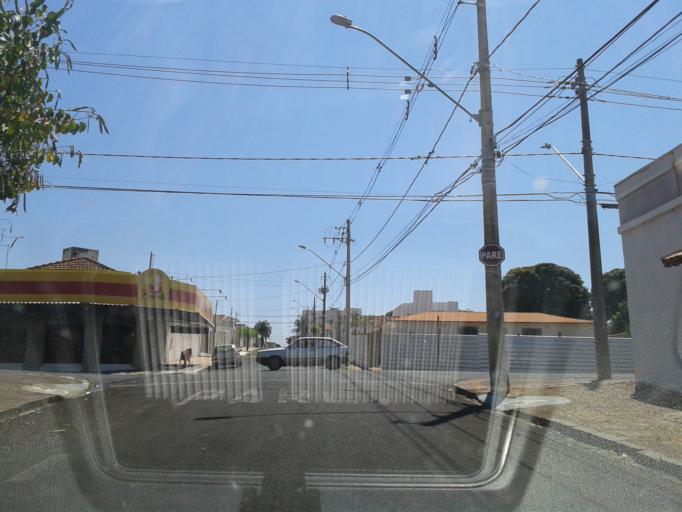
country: BR
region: Minas Gerais
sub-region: Araguari
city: Araguari
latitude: -18.6444
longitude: -48.1903
